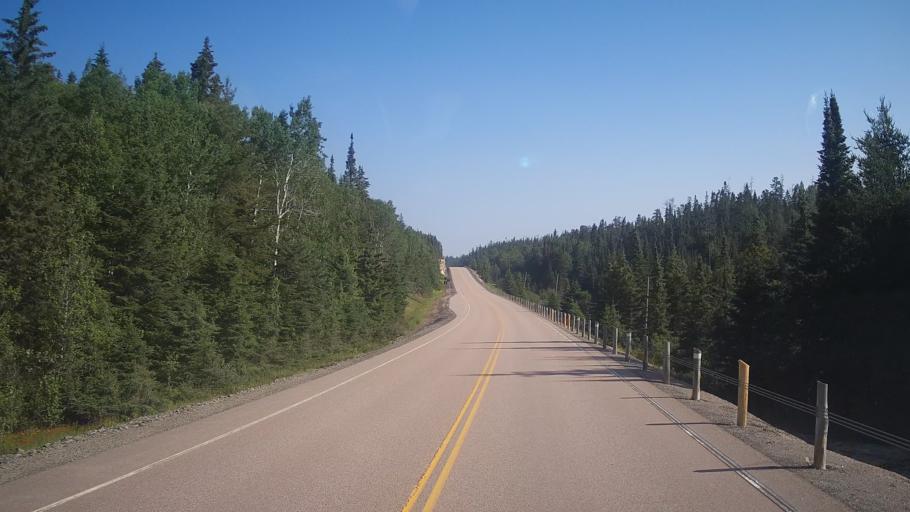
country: CA
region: Ontario
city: Rayside-Balfour
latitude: 46.9959
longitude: -81.6323
